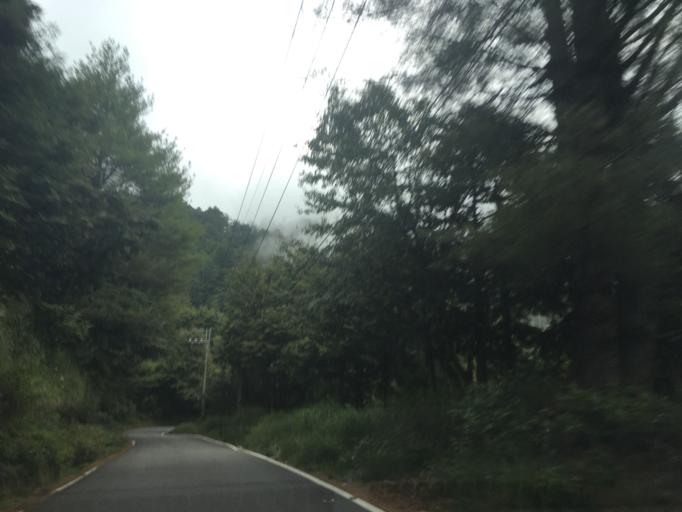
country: TW
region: Taiwan
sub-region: Nantou
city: Puli
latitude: 24.2747
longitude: 121.0319
